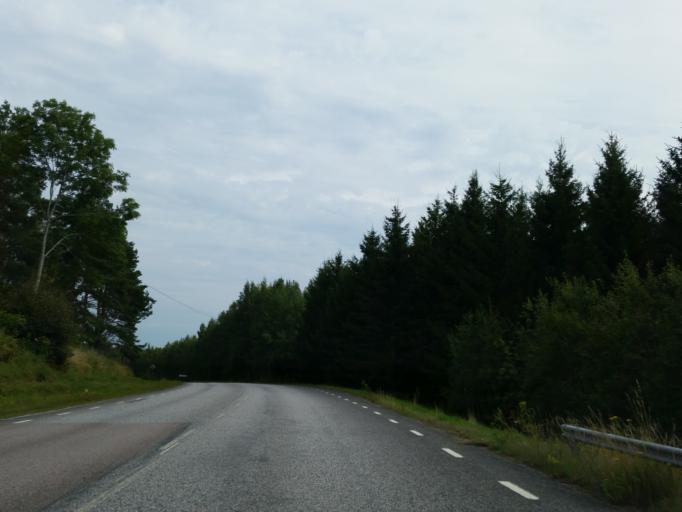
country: SE
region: Soedermanland
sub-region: Strangnas Kommun
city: Mariefred
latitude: 59.2202
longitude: 17.2302
